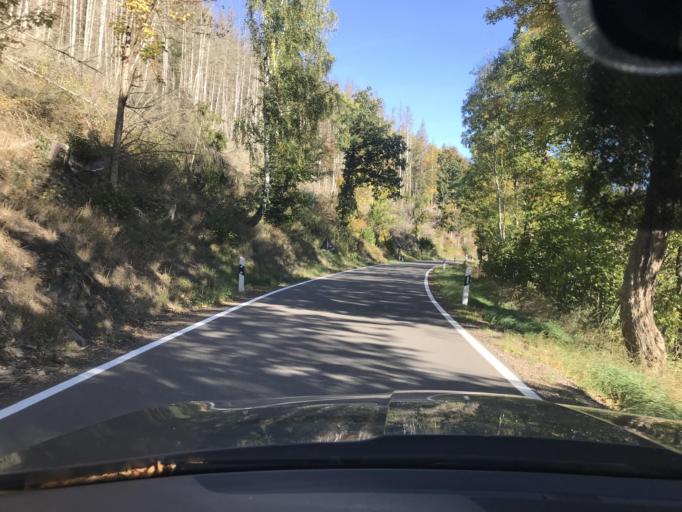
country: DE
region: Saxony-Anhalt
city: Friedrichsbrunn
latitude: 51.6878
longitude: 10.9665
